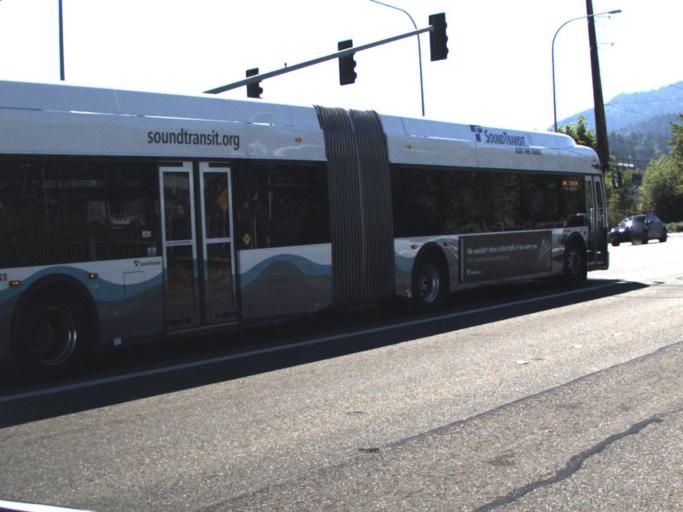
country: US
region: Washington
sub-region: King County
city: Issaquah
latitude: 47.5434
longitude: -122.0628
